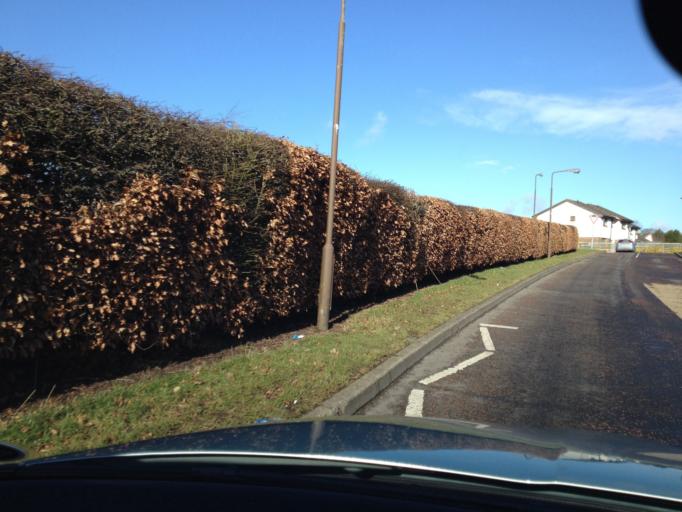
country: GB
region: Scotland
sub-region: West Lothian
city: Livingston
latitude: 55.8865
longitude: -3.5385
